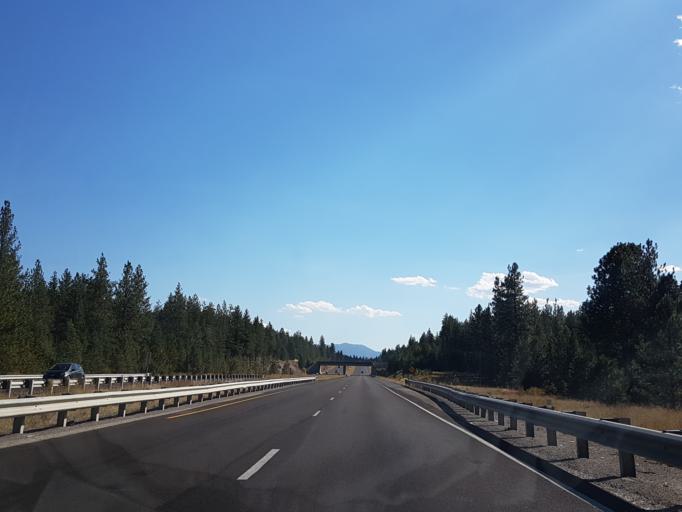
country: US
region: Montana
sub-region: Mineral County
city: Superior
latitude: 47.1301
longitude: -114.7964
